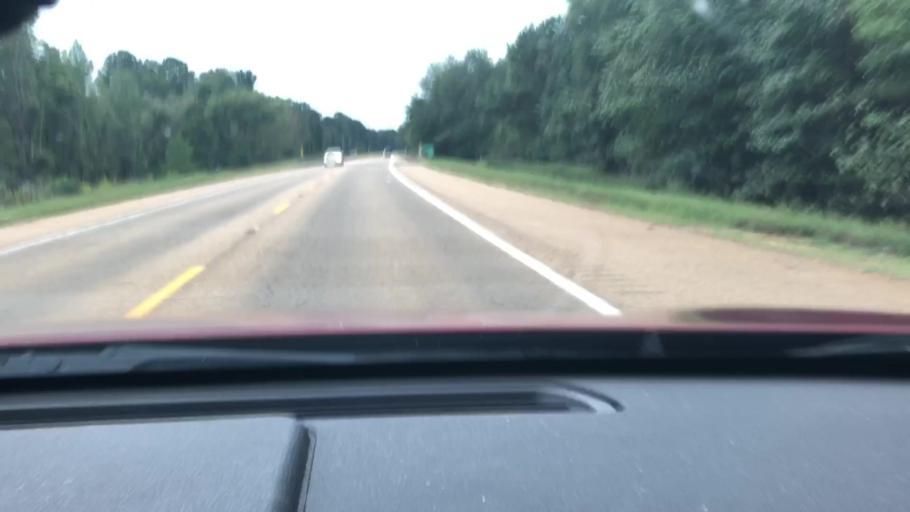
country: US
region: Arkansas
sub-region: Lafayette County
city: Stamps
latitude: 33.3589
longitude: -93.4159
